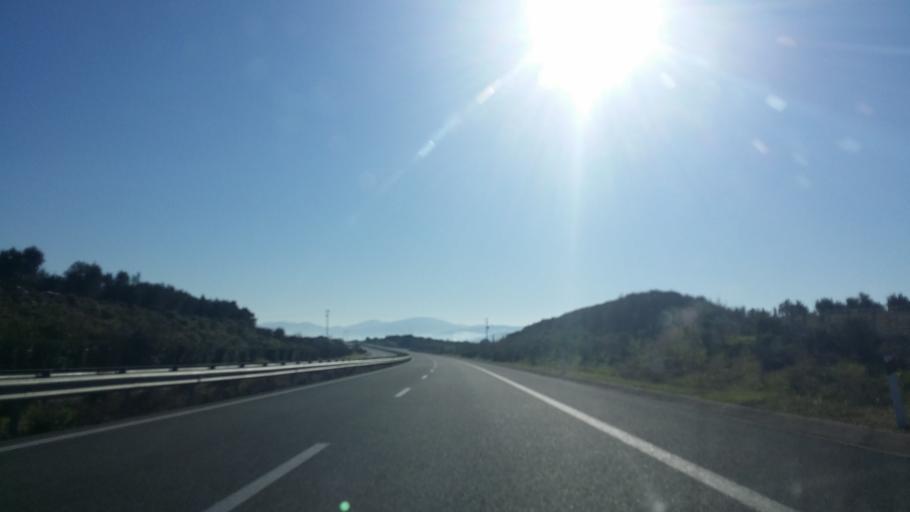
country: GR
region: West Greece
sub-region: Nomos Aitolias kai Akarnanias
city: Fitiai
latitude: 38.6773
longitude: 21.2214
